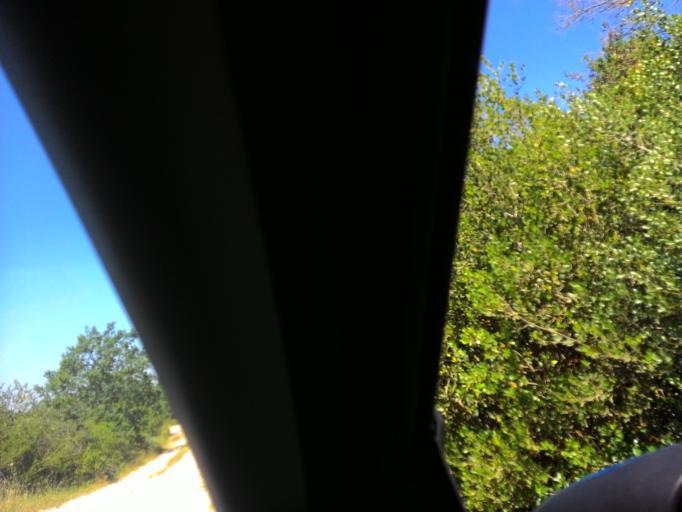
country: IT
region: Apulia
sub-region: Provincia di Bari
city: Noci
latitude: 40.8176
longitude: 17.1338
